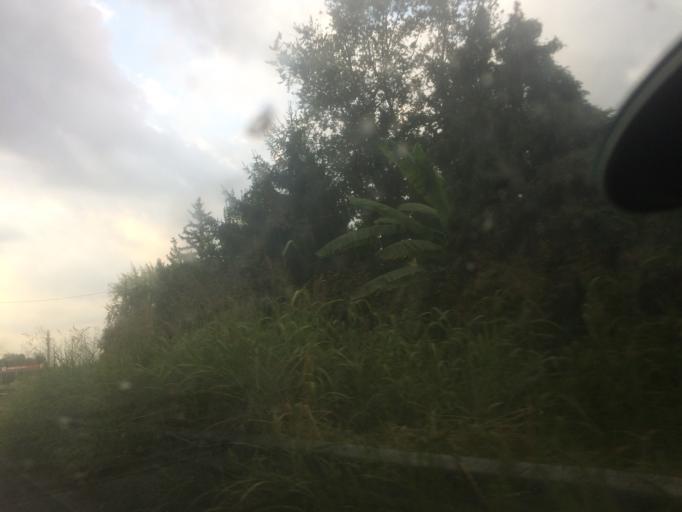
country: IT
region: Tuscany
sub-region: Provincia di Massa-Carrara
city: Massa
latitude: 44.0203
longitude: 10.0964
